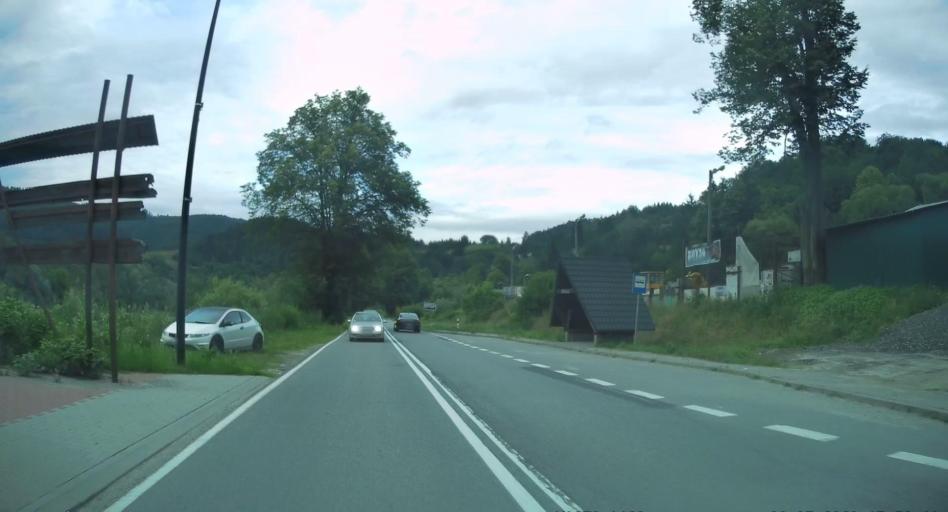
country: PL
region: Lesser Poland Voivodeship
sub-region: Powiat nowosadecki
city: Piwniczna-Zdroj
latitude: 49.3686
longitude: 20.7855
